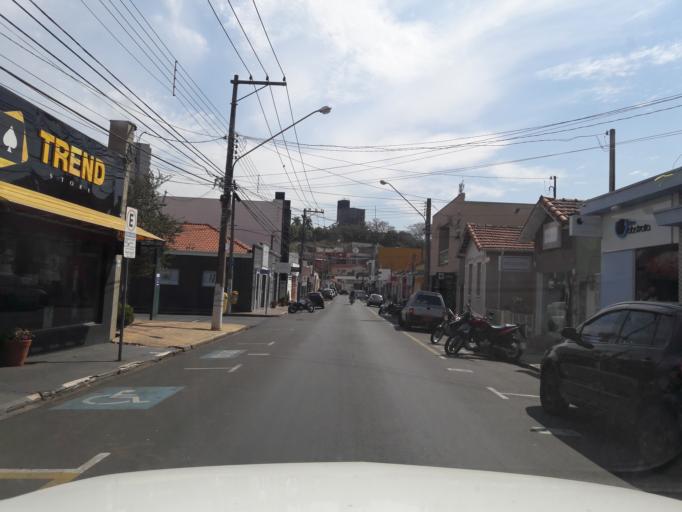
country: BR
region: Sao Paulo
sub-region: Moji-Guacu
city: Mogi-Gaucu
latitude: -22.3701
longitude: -46.9411
